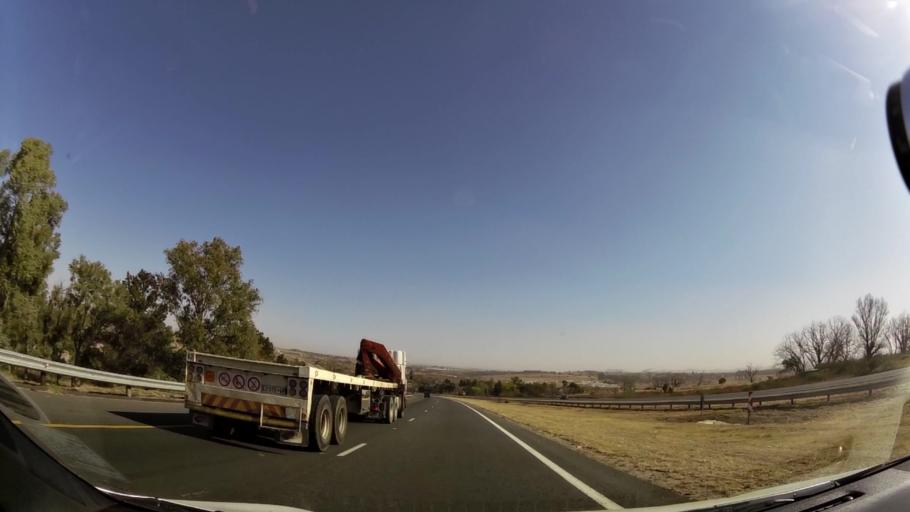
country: ZA
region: Gauteng
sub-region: City of Johannesburg Metropolitan Municipality
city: Diepsloot
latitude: -25.9433
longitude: 27.9623
